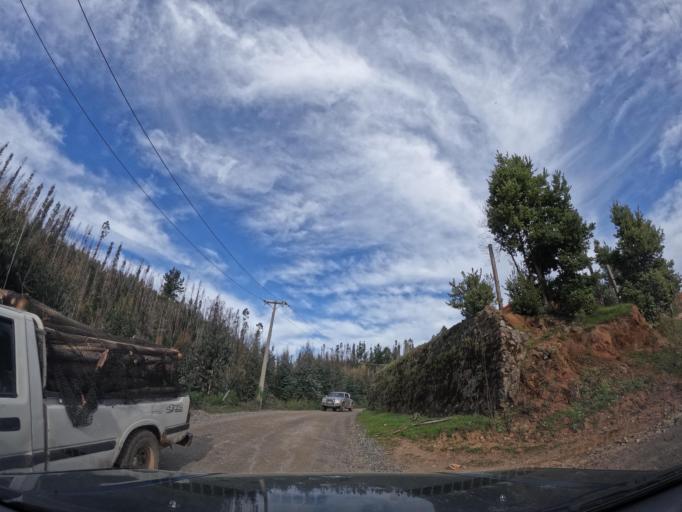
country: CL
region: Biobio
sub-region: Provincia de Concepcion
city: Chiguayante
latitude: -37.0131
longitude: -72.9093
